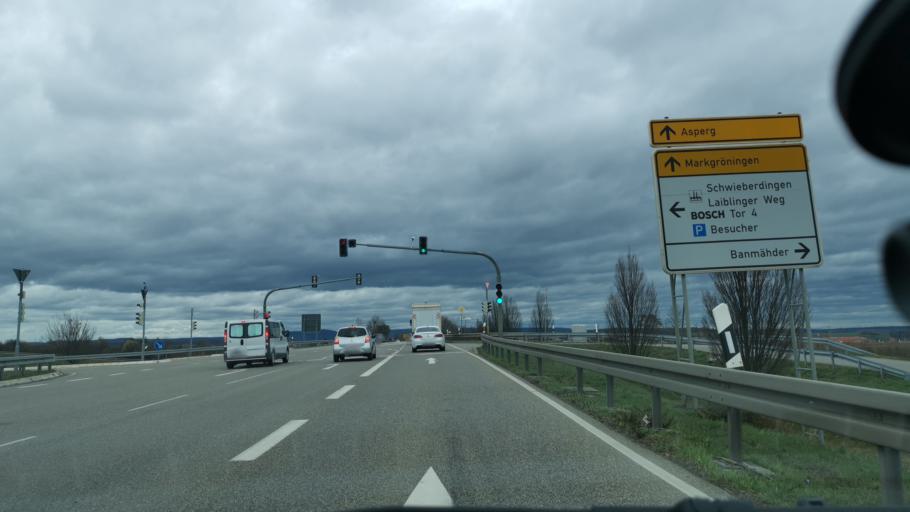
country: DE
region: Baden-Wuerttemberg
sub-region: Regierungsbezirk Stuttgart
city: Schwieberdingen
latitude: 48.8854
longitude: 9.0943
